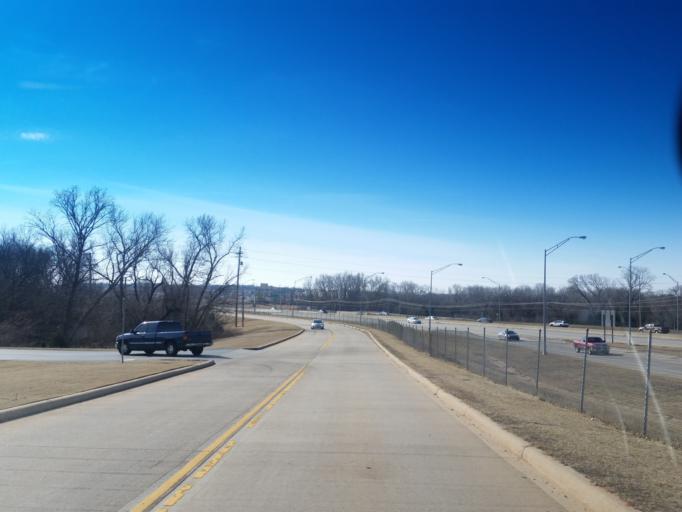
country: US
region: Oklahoma
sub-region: Oklahoma County
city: Edmond
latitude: 35.6499
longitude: -97.4237
